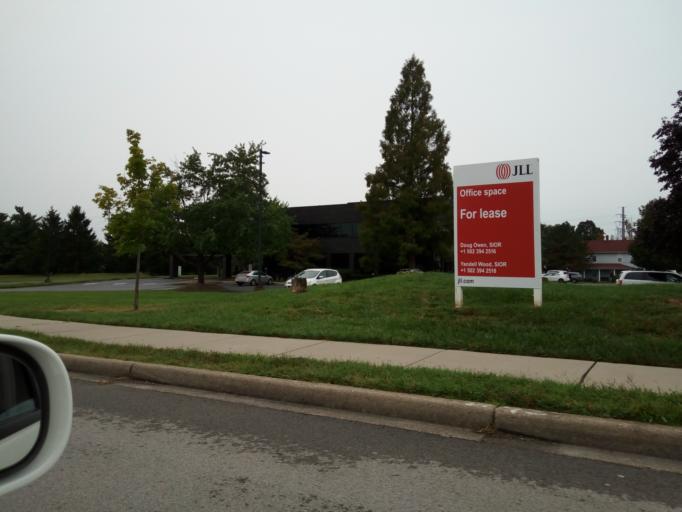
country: US
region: Kentucky
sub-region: Jefferson County
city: Middletown
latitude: 38.2429
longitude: -85.5148
